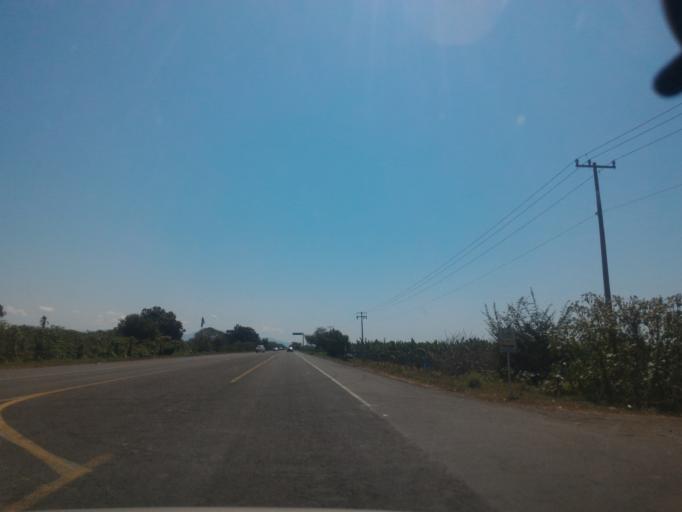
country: MX
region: Colima
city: Tecoman
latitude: 18.8188
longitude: -103.8085
